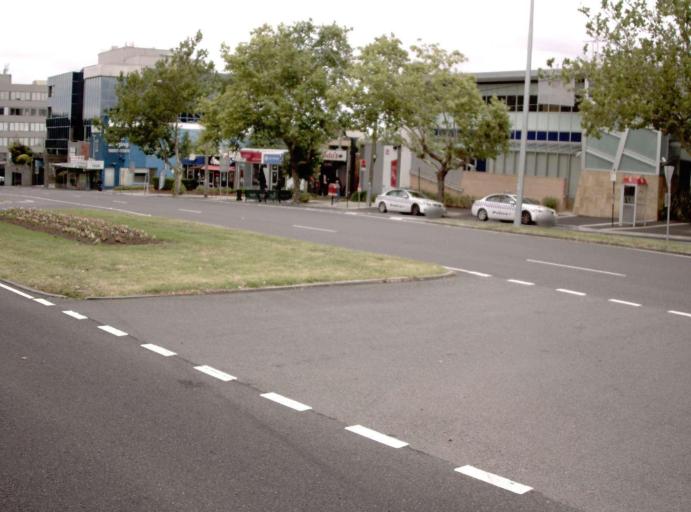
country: AU
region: Victoria
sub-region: Whitehorse
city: Box Hill
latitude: -37.8186
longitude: 145.1275
